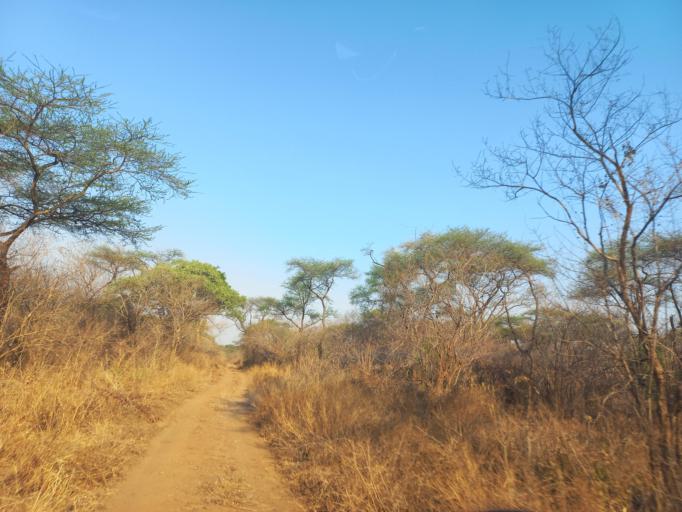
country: ZM
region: Lusaka
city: Luangwa
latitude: -15.4175
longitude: 30.2481
